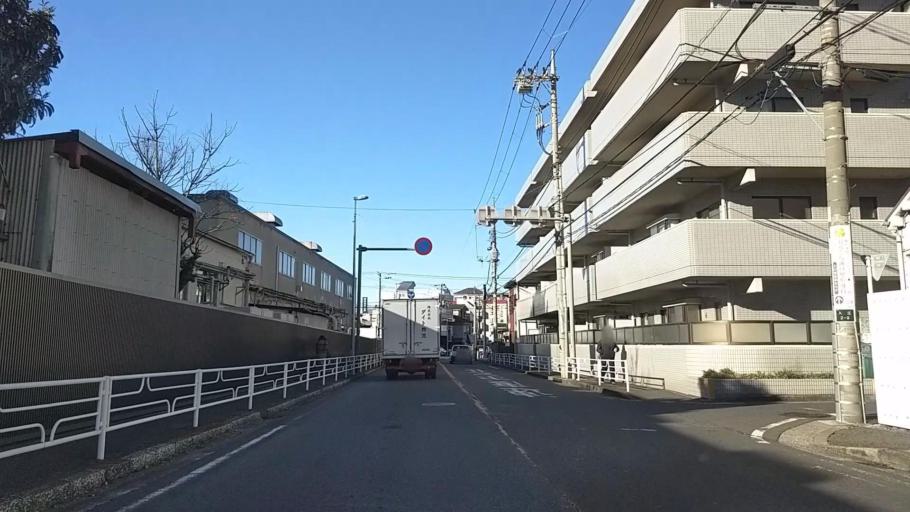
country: JP
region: Kanagawa
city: Yokohama
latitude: 35.4908
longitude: 139.6494
